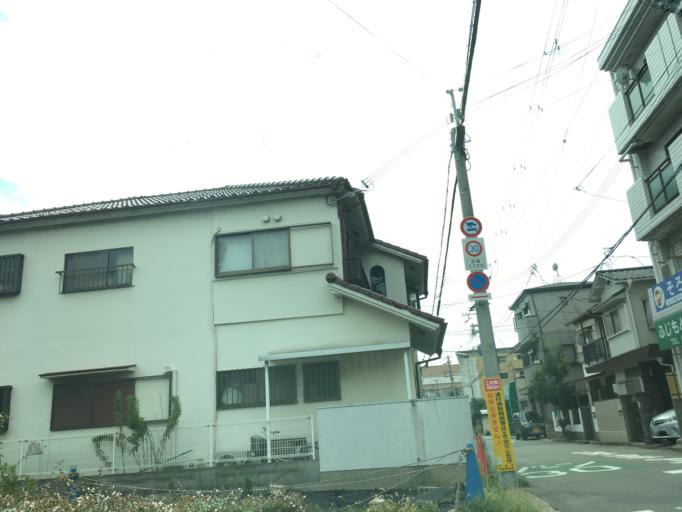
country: JP
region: Hyogo
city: Ashiya
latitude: 34.7302
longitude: 135.3172
